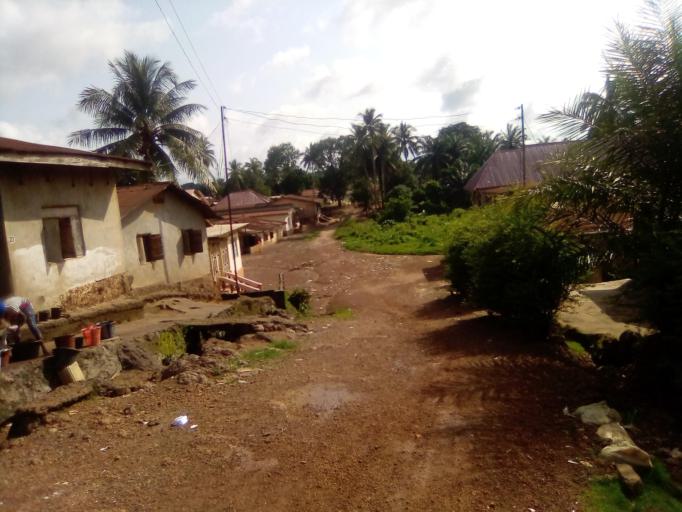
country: SL
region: Southern Province
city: Bo
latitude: 7.9731
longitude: -11.7298
